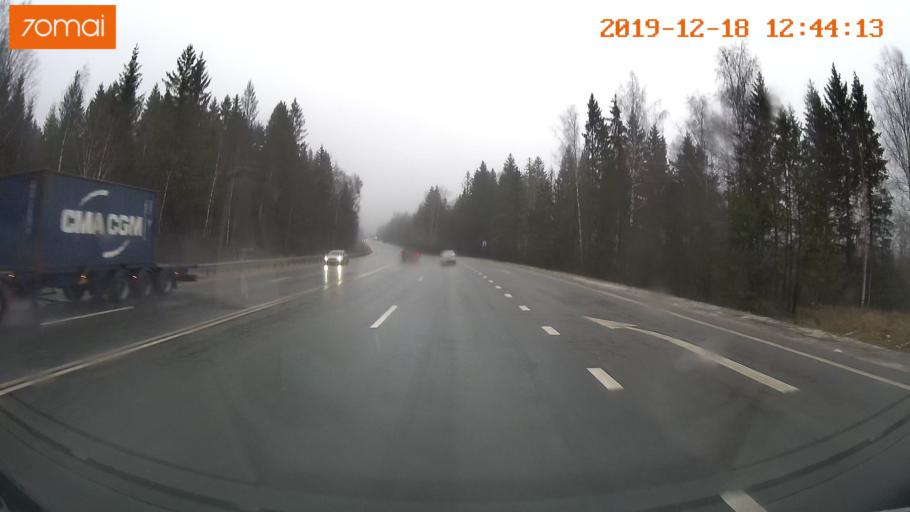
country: RU
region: Moskovskaya
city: Vysokovsk
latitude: 56.2169
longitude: 36.6472
